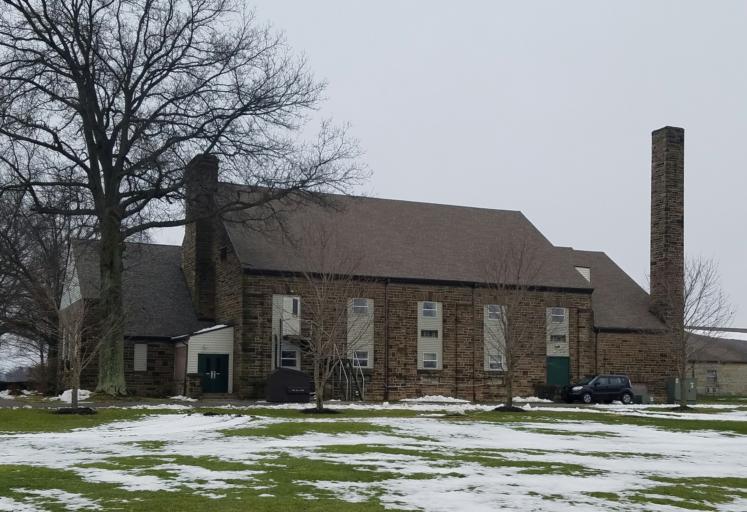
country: US
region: Pennsylvania
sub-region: Mercer County
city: Mercer
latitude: 41.3174
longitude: -80.2625
